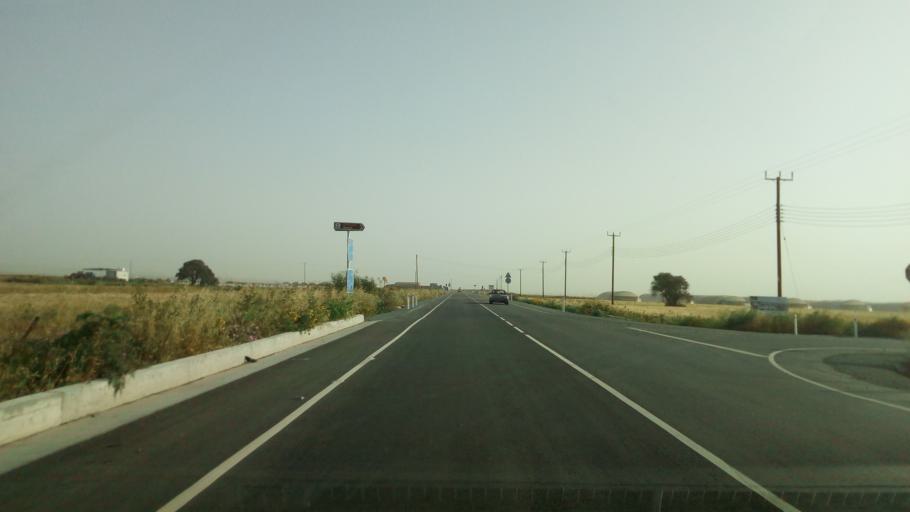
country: CY
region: Larnaka
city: Tersefanou
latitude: 34.8152
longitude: 33.5252
